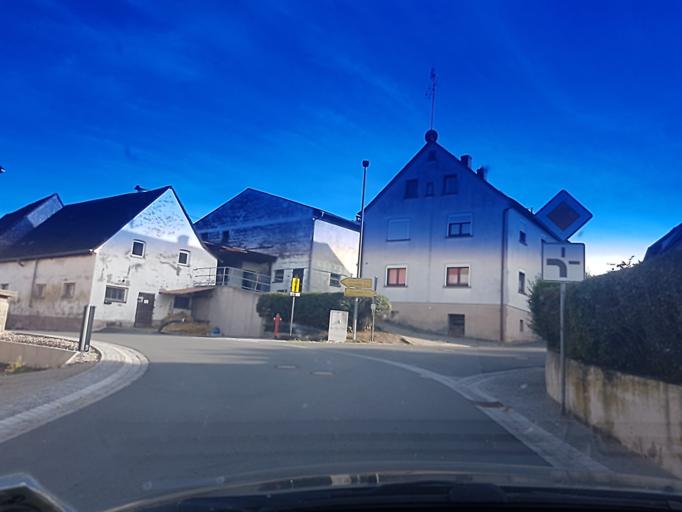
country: DE
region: Bavaria
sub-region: Upper Franconia
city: Schlusselfeld
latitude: 49.7667
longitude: 10.6573
